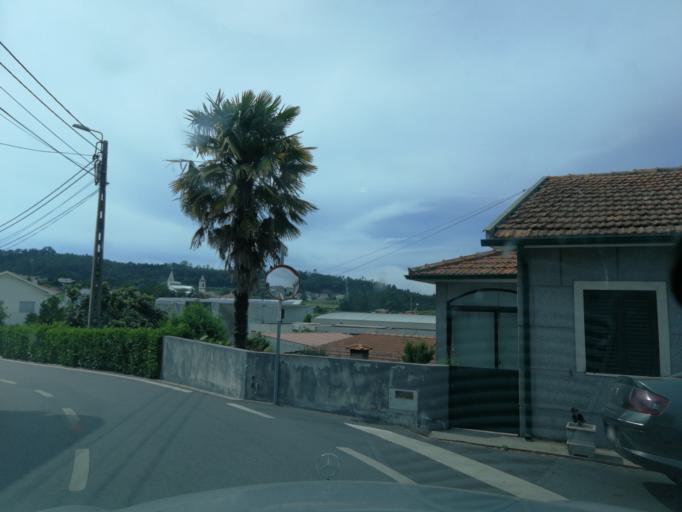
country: PT
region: Braga
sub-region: Vila Nova de Famalicao
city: Calendario
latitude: 41.4102
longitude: -8.5373
